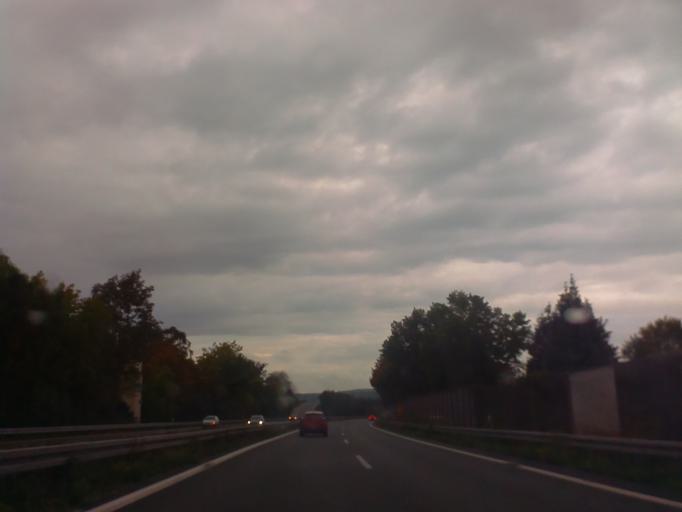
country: DE
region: Bavaria
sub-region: Regierungsbezirk Unterfranken
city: Elsenfeld
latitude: 49.8414
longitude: 9.1501
